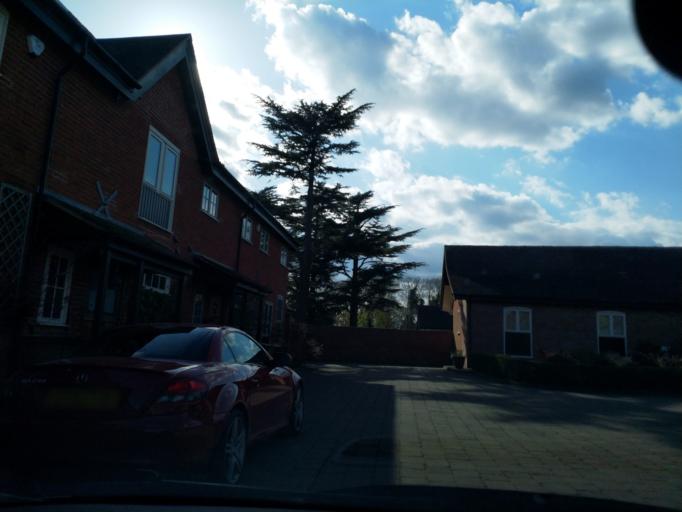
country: GB
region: England
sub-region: Warwickshire
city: Wellesbourne Mountford
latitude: 52.1873
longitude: -1.5520
